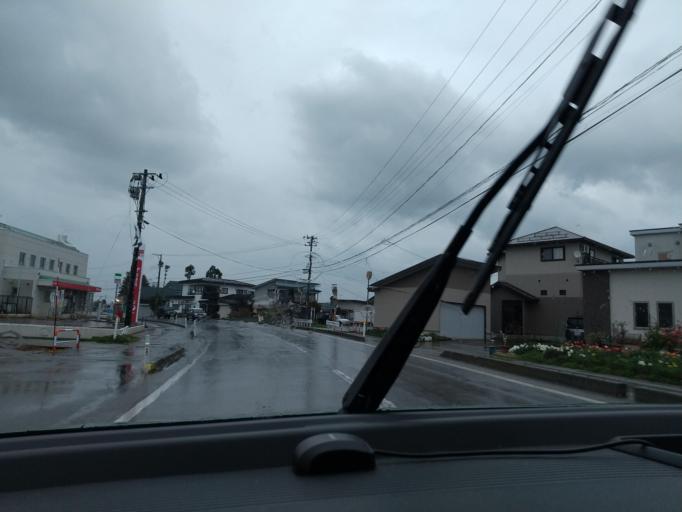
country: JP
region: Akita
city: Yokotemachi
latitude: 39.3890
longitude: 140.5333
